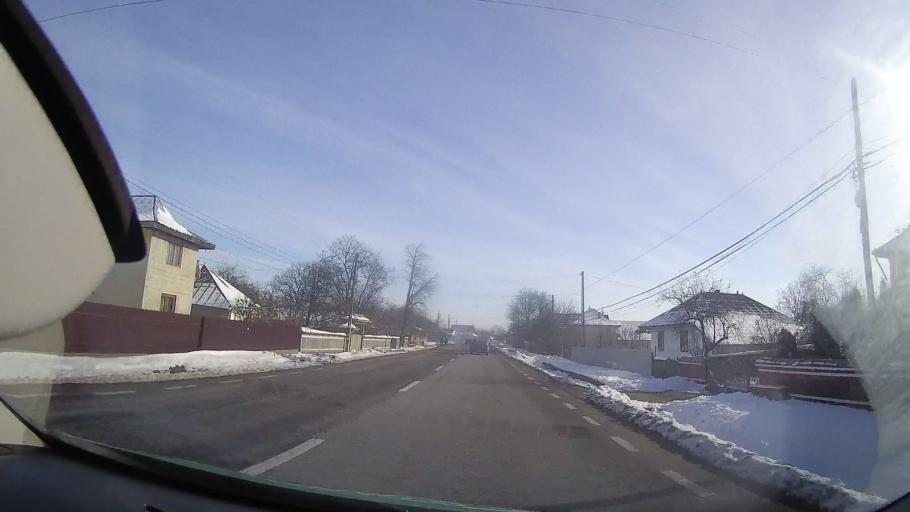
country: RO
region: Neamt
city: Bodesti
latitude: 47.0535
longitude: 26.3991
